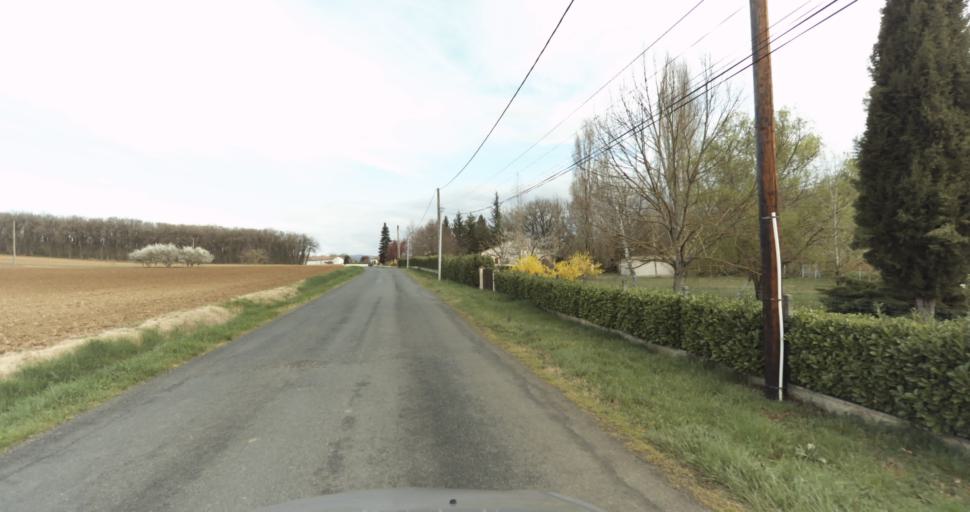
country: FR
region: Midi-Pyrenees
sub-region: Departement du Tarn
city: Puygouzon
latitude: 43.9029
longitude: 2.1846
